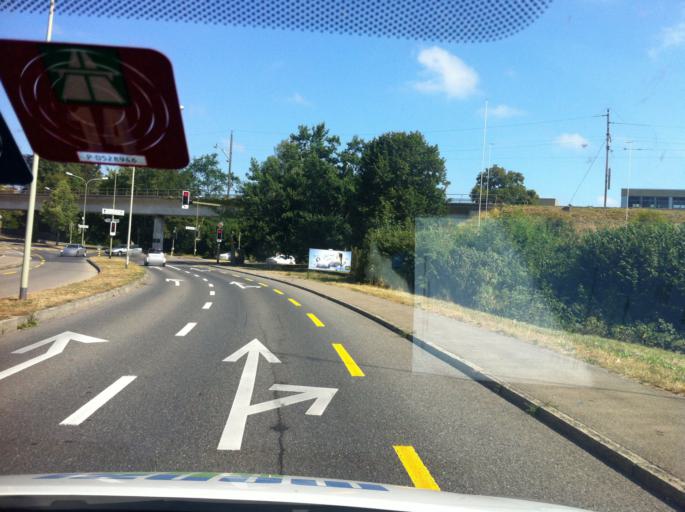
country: CH
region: Zurich
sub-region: Bezirk Buelach
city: Bulach
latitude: 47.5210
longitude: 8.5422
